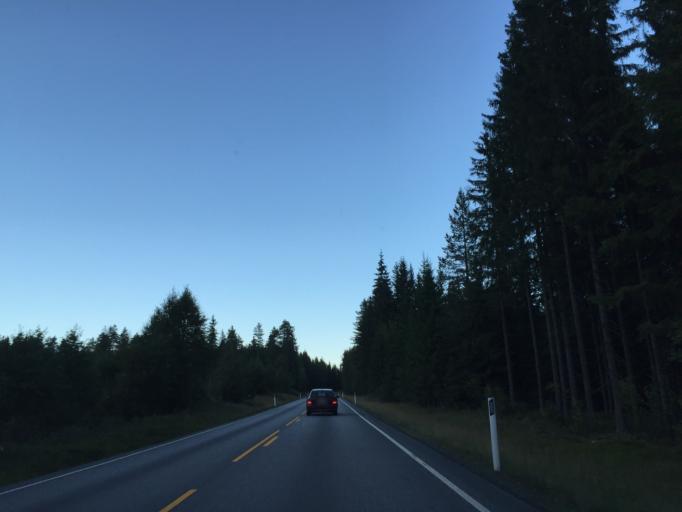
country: NO
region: Hedmark
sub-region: Nord-Odal
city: Sand
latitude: 60.4980
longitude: 11.5018
